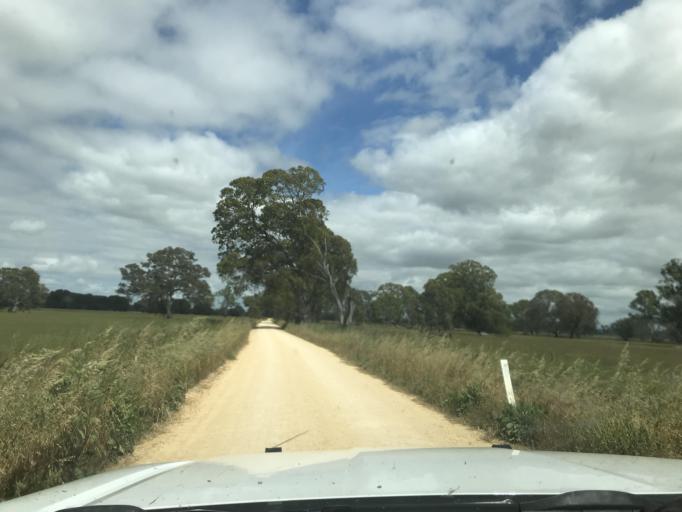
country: AU
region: South Australia
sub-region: Naracoorte and Lucindale
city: Naracoorte
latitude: -37.0059
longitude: 141.1124
